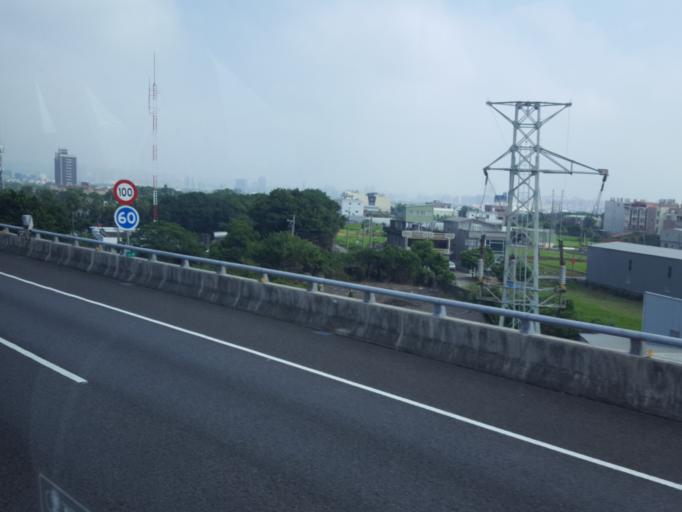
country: TW
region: Taiwan
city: Taoyuan City
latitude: 25.0003
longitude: 121.2506
